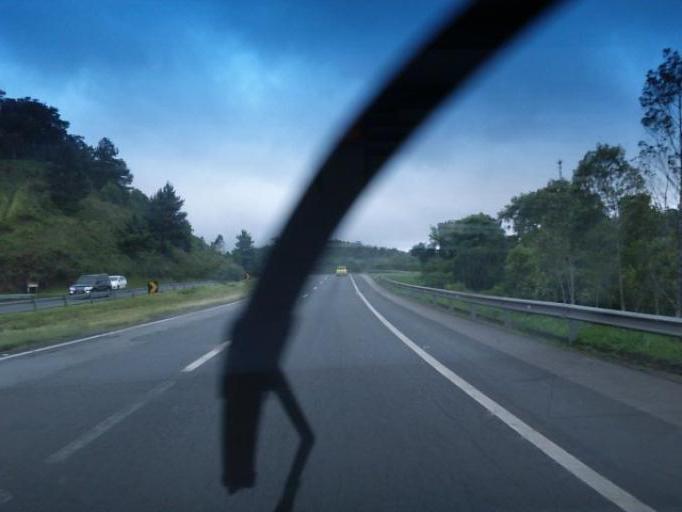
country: BR
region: Parana
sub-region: Antonina
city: Antonina
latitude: -25.0678
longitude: -48.5825
